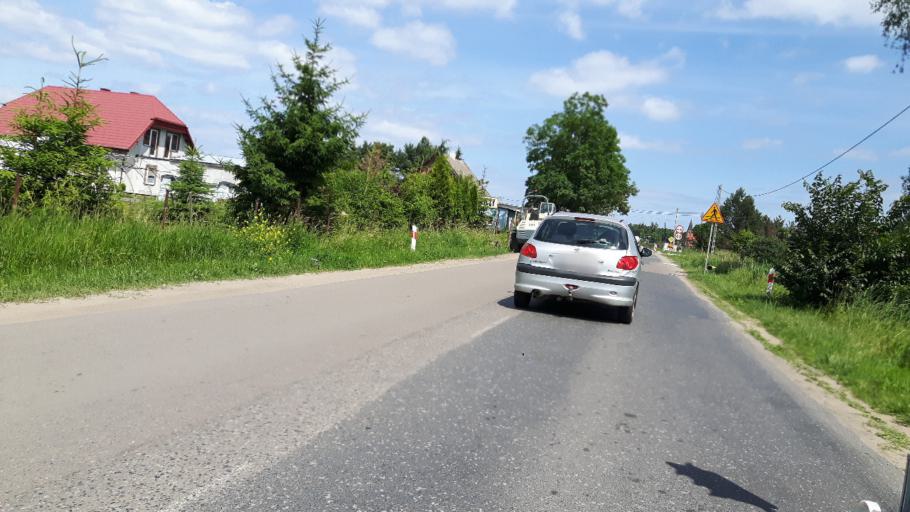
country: PL
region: Pomeranian Voivodeship
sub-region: Powiat gdanski
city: Cedry Wielkie
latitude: 54.3374
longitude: 18.8231
